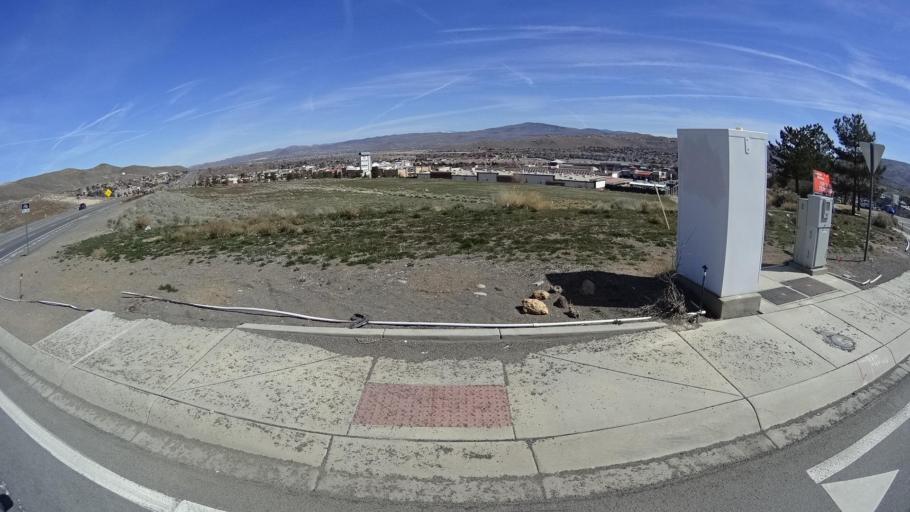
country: US
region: Nevada
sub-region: Washoe County
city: Sun Valley
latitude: 39.5767
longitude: -119.7456
